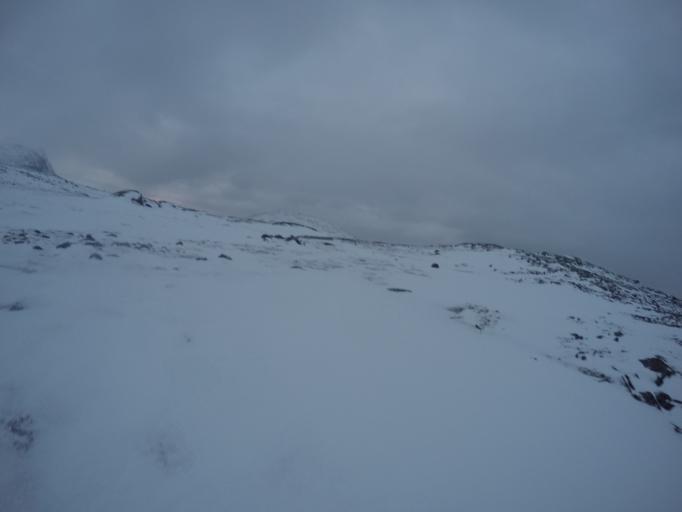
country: GL
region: Sermersooq
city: Nuuk
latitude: 64.1377
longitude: -51.6752
